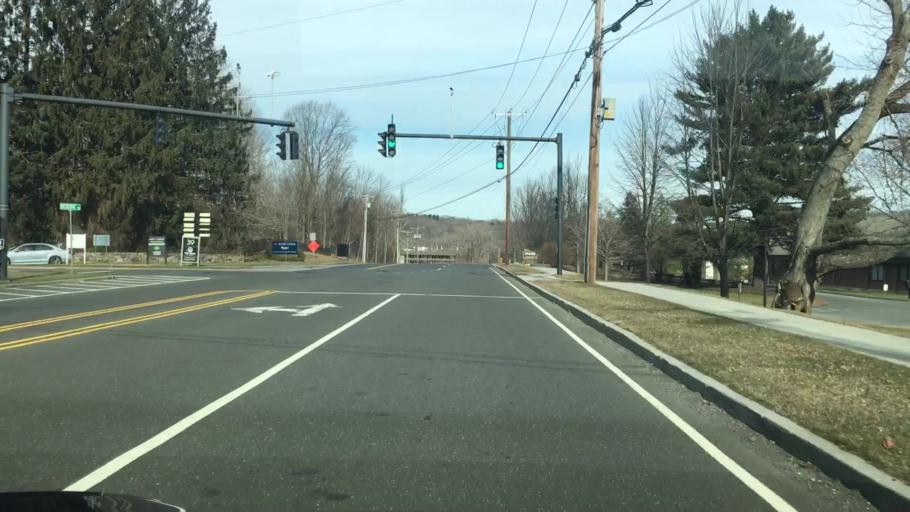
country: US
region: Connecticut
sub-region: Fairfield County
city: Danbury
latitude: 41.3850
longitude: -73.5152
